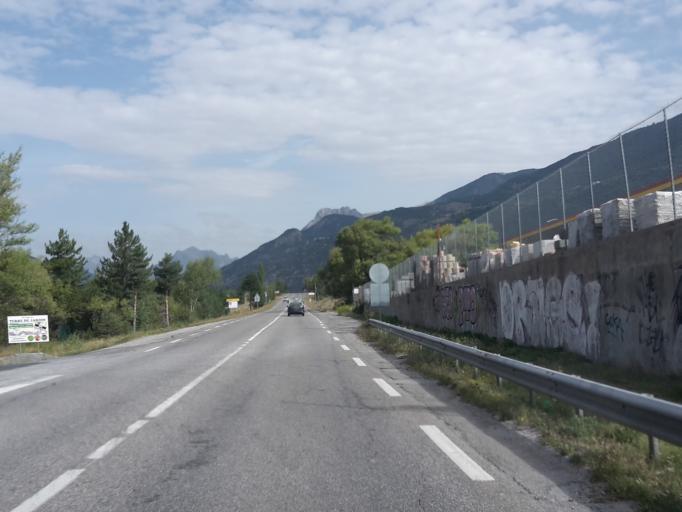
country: FR
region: Provence-Alpes-Cote d'Azur
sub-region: Departement des Hautes-Alpes
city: Guillestre
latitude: 44.6840
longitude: 6.6146
